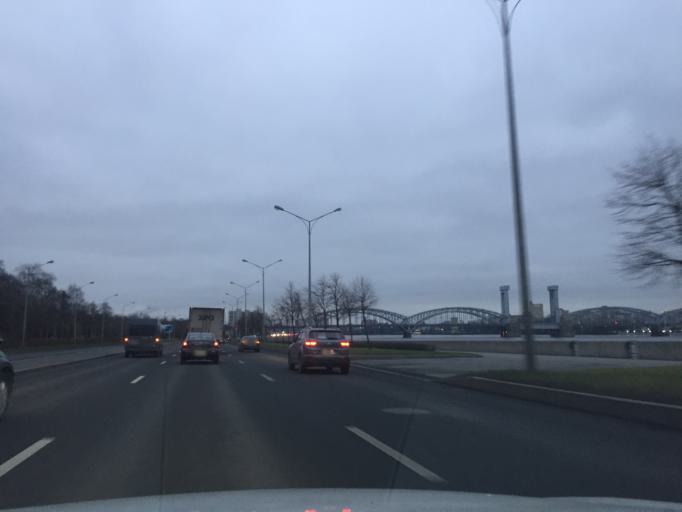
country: RU
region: St.-Petersburg
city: Centralniy
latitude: 59.9211
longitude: 30.4079
